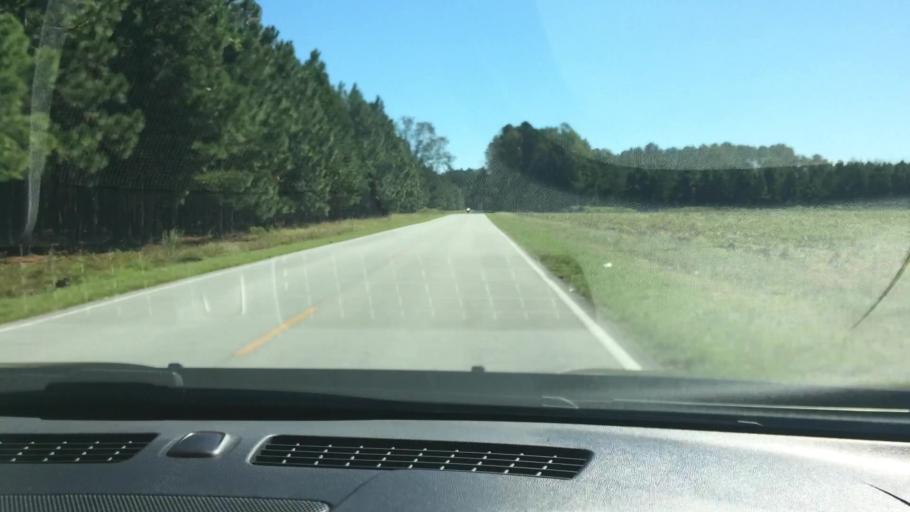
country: US
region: North Carolina
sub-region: Pitt County
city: Grifton
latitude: 35.3359
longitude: -77.3055
